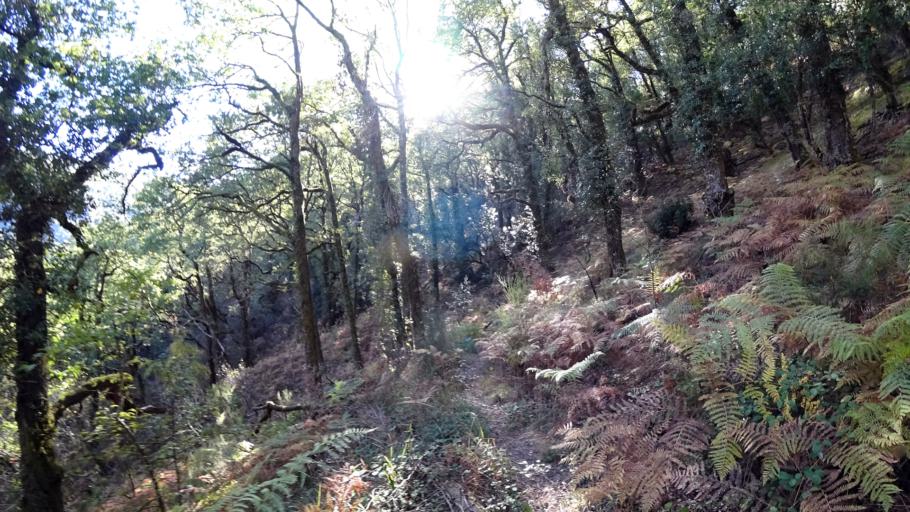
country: ES
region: Galicia
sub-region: Provincia de Ourense
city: Lobios
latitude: 41.7992
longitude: -8.1526
